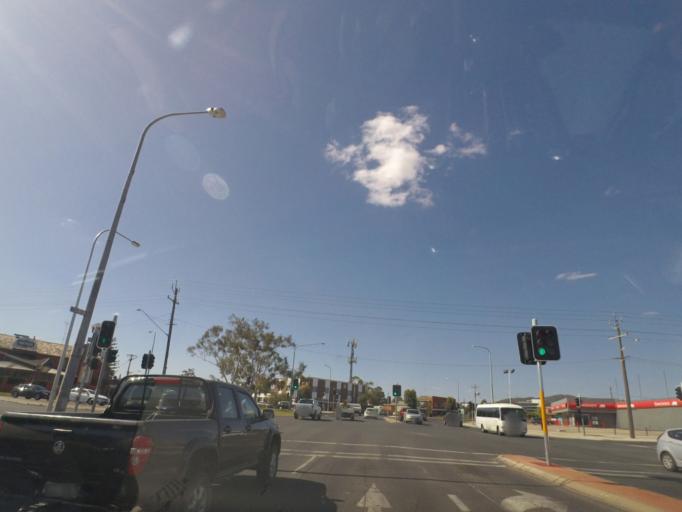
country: AU
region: New South Wales
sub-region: Albury Municipality
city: Lavington
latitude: -36.0528
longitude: 146.9335
